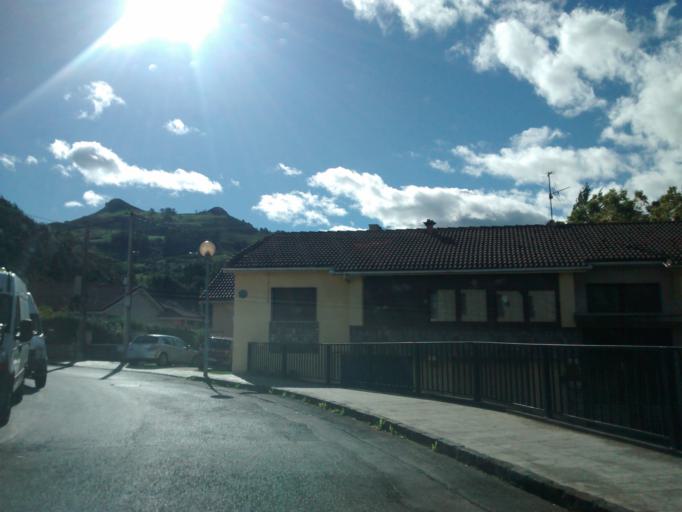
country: ES
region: Cantabria
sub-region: Provincia de Cantabria
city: Lierganes
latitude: 43.3450
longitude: -3.7428
